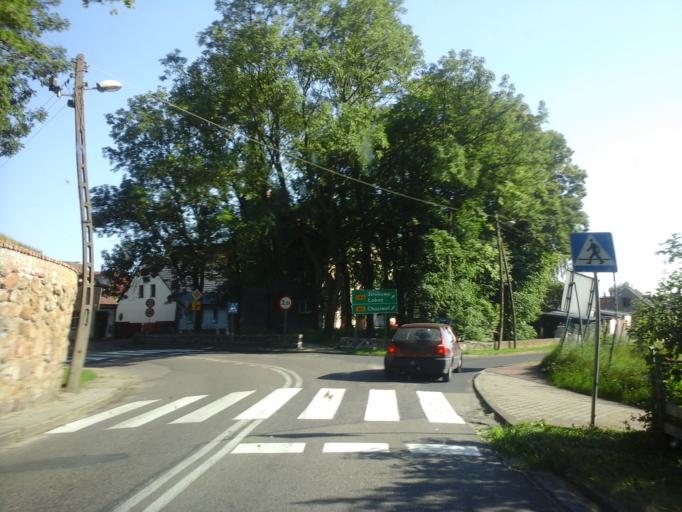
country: PL
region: West Pomeranian Voivodeship
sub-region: Powiat lobeski
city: Dobra
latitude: 53.5880
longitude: 15.3092
